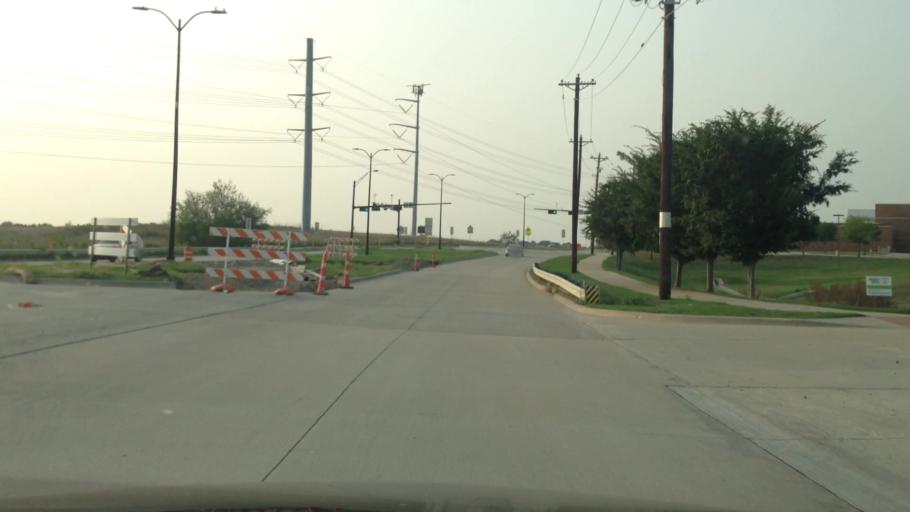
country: US
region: Texas
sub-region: Collin County
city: Frisco
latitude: 33.1239
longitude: -96.8473
